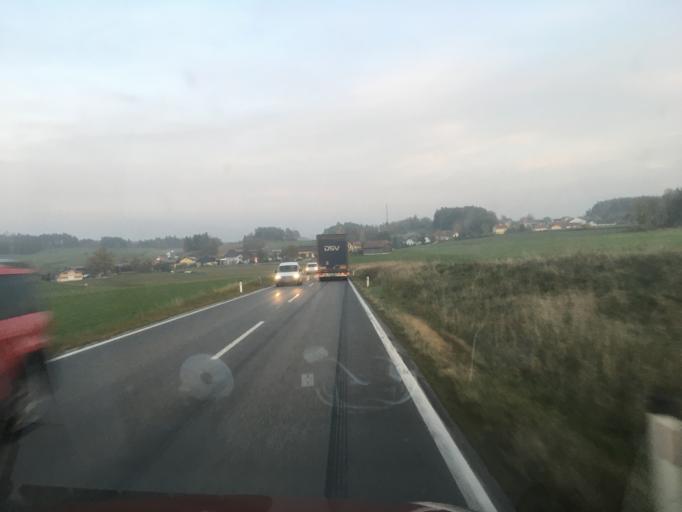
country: AT
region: Lower Austria
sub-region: Politischer Bezirk Zwettl
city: Gross-Gerungs
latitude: 48.5577
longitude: 15.0095
